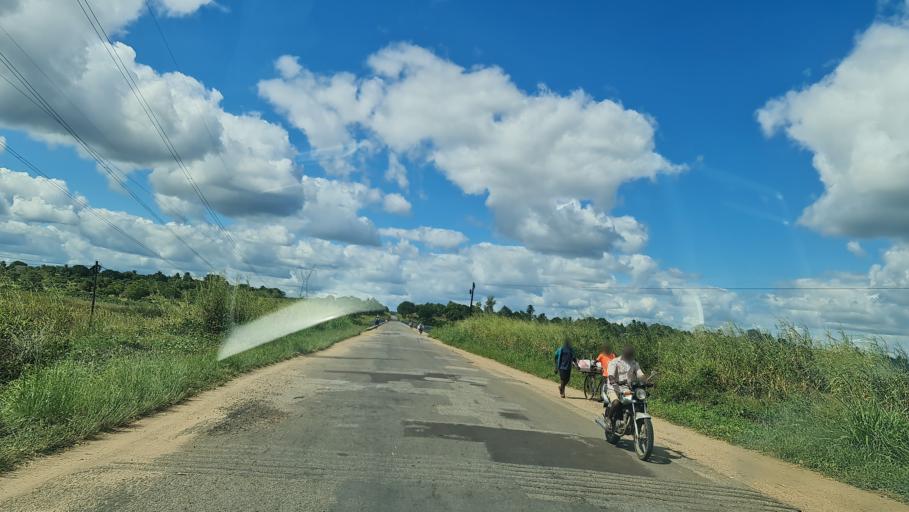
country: MZ
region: Zambezia
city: Quelimane
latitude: -17.5250
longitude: 36.2703
